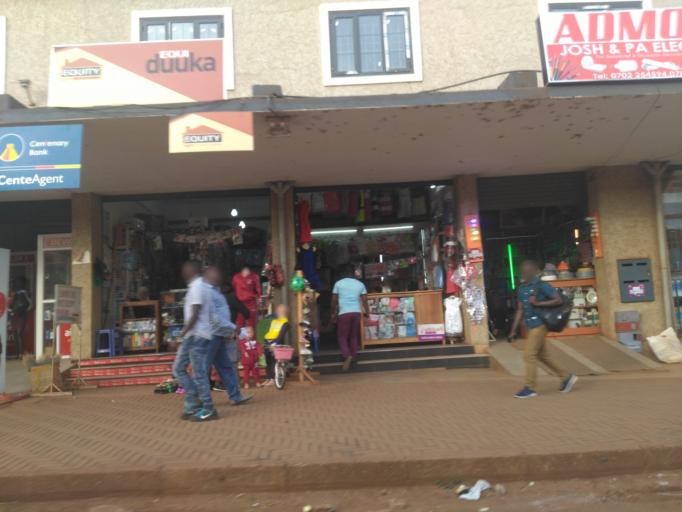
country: UG
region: Eastern Region
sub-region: Jinja District
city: Jinja
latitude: 0.4303
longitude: 33.2120
